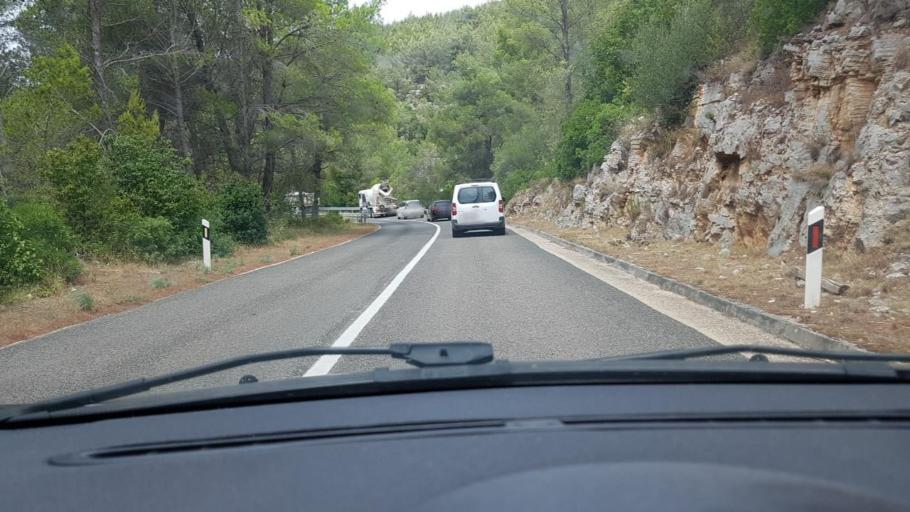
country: HR
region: Dubrovacko-Neretvanska
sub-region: Grad Dubrovnik
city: Vela Luka
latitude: 42.9497
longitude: 16.7912
